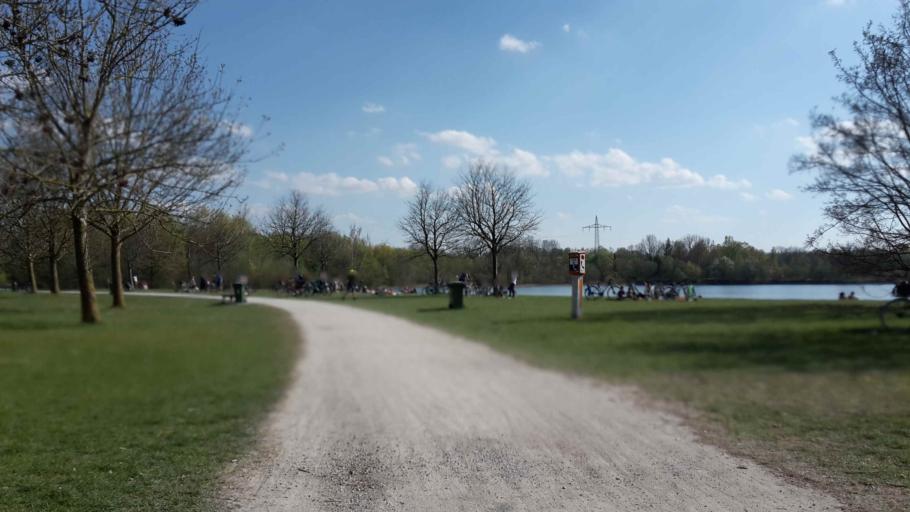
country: DE
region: Bavaria
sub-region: Upper Bavaria
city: Karlsfeld
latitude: 48.2005
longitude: 11.4208
